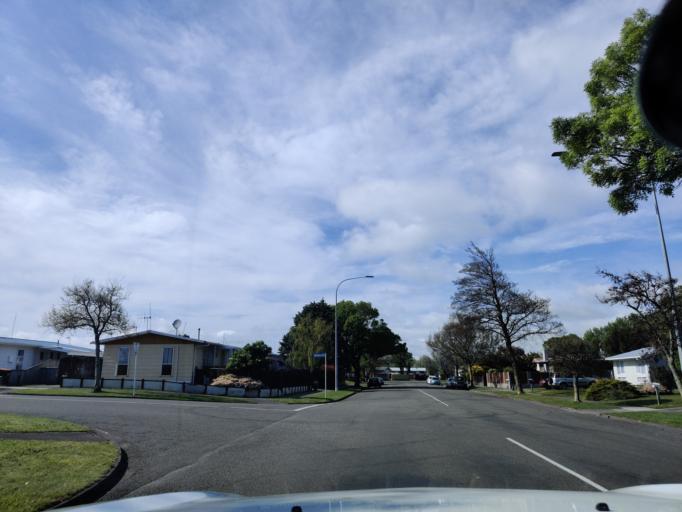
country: NZ
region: Manawatu-Wanganui
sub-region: Palmerston North City
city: Palmerston North
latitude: -40.3312
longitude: 175.6405
